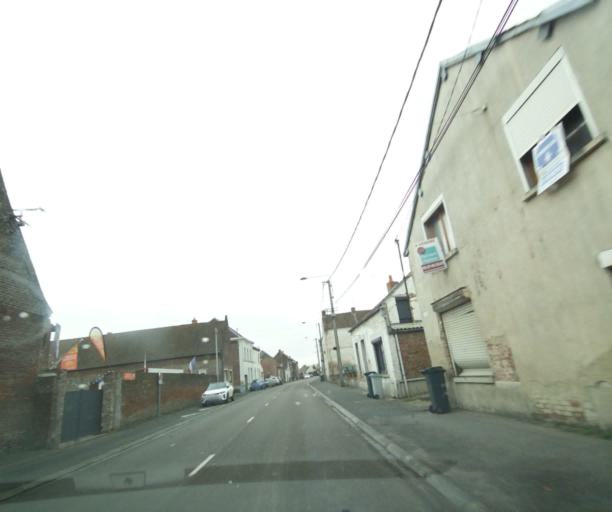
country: FR
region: Nord-Pas-de-Calais
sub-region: Departement du Nord
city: Crespin
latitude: 50.4199
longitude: 3.6612
